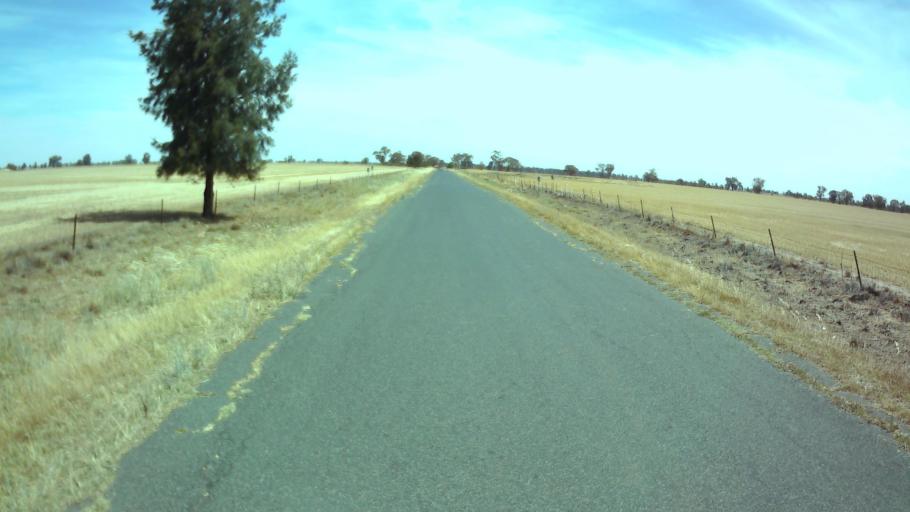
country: AU
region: New South Wales
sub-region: Weddin
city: Grenfell
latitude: -33.9312
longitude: 147.7622
